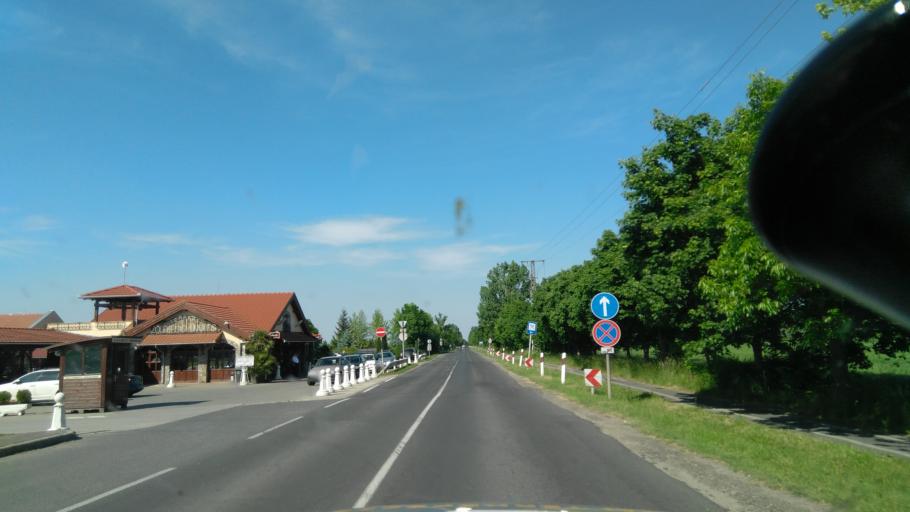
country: HU
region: Bekes
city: Sarkad
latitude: 46.7180
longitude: 21.3324
